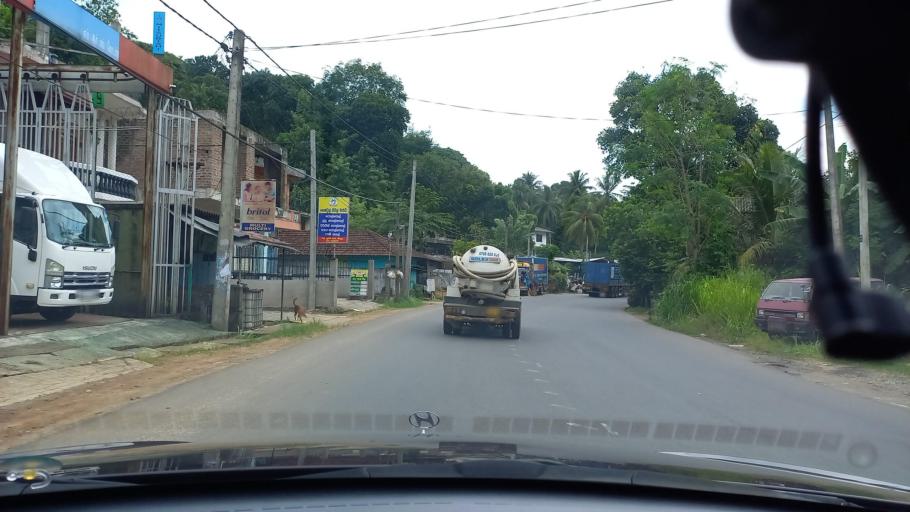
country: LK
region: Central
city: Kadugannawa
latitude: 7.2476
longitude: 80.4730
